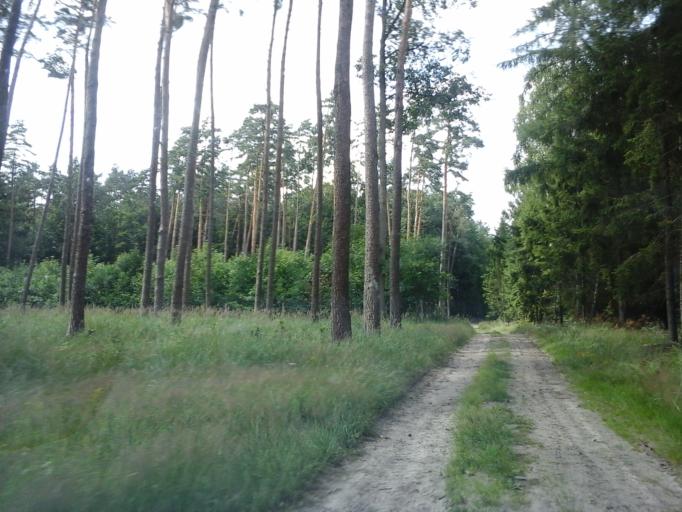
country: PL
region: West Pomeranian Voivodeship
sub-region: Powiat choszczenski
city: Bierzwnik
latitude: 53.0688
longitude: 15.6765
